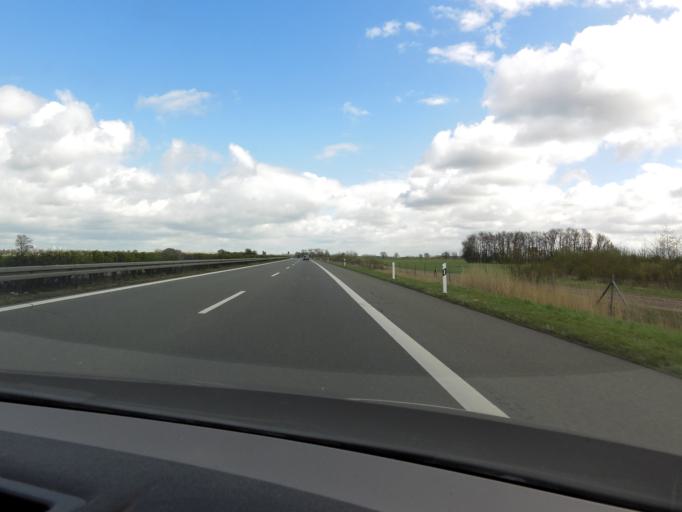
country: DE
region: Mecklenburg-Vorpommern
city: Franzburg
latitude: 54.0757
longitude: 12.8821
